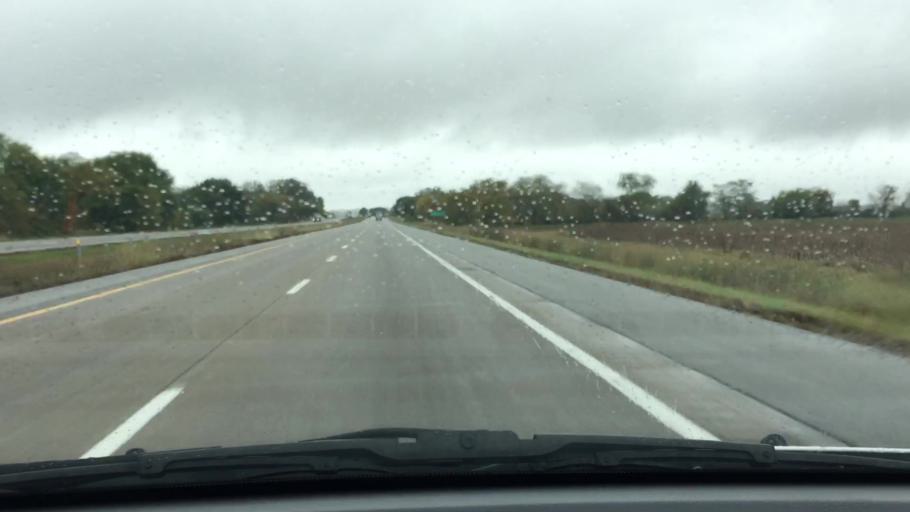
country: US
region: Iowa
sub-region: Jasper County
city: Colfax
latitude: 41.6952
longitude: -93.1916
